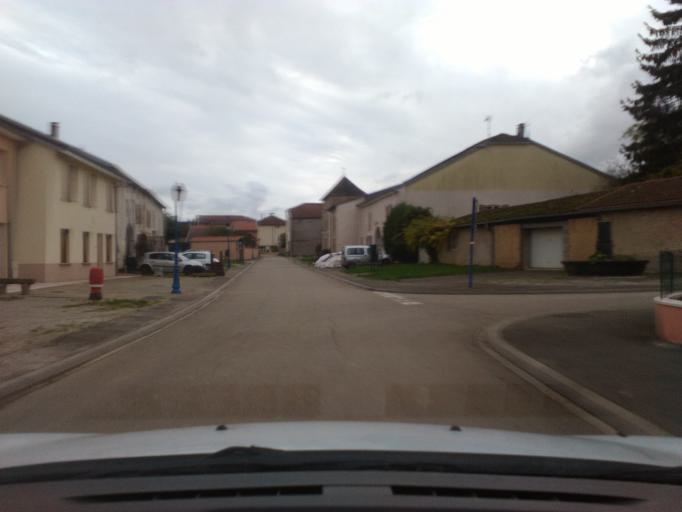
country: FR
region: Lorraine
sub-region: Departement des Vosges
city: Mirecourt
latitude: 48.3328
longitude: 6.0587
